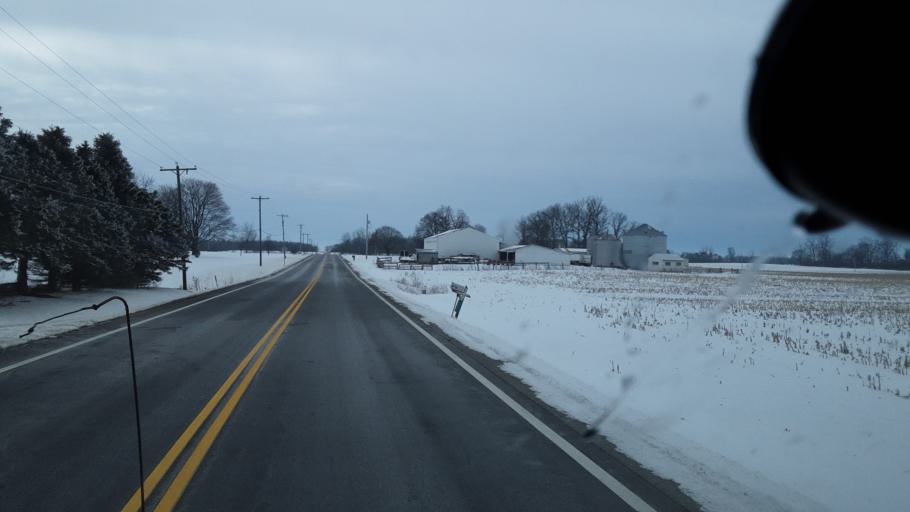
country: US
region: Ohio
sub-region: Madison County
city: London
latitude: 39.8247
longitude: -83.4656
